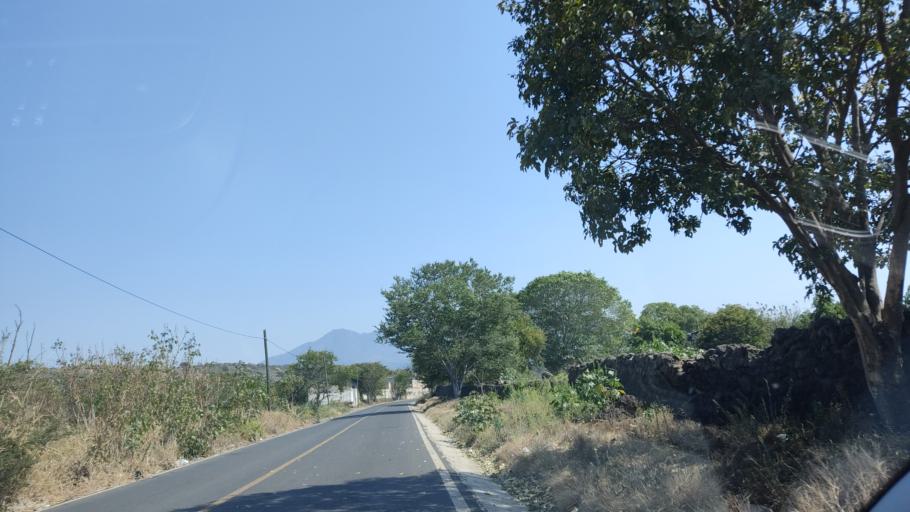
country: MX
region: Nayarit
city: Puga
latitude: 21.5378
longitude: -104.8106
